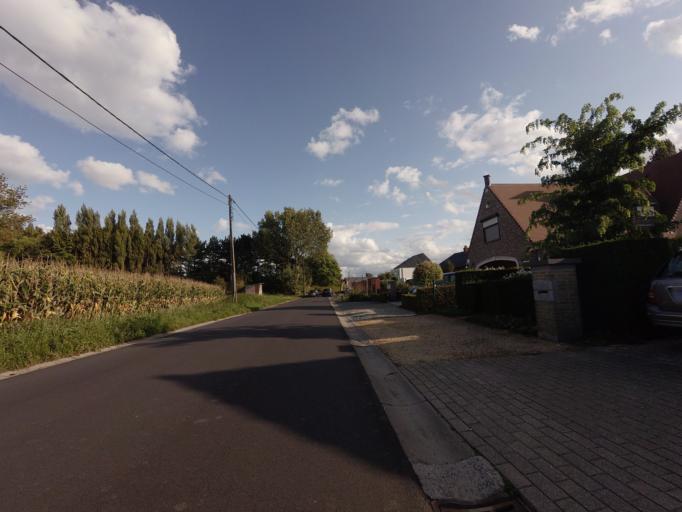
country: BE
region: Flanders
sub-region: Provincie Vlaams-Brabant
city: Londerzeel
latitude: 51.0014
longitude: 4.3330
